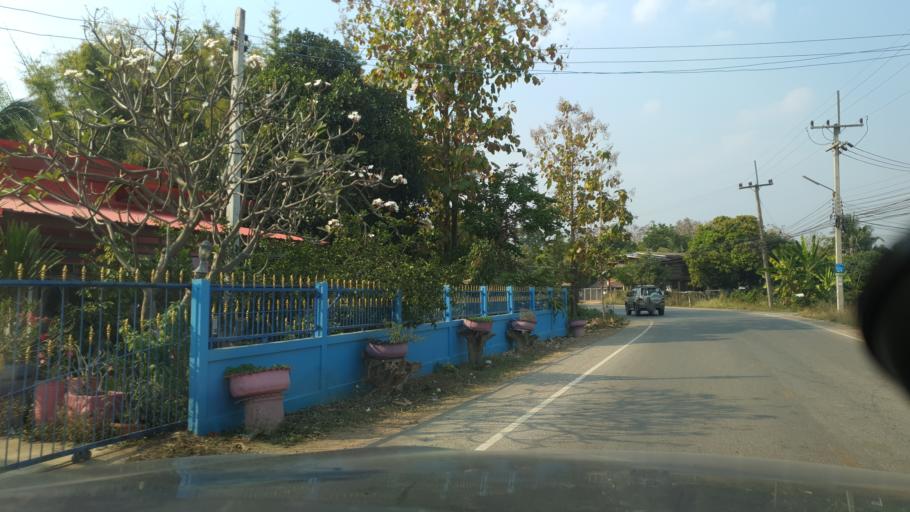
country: TH
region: Sukhothai
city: Ban Dan Lan Hoi
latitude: 17.1157
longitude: 99.5386
